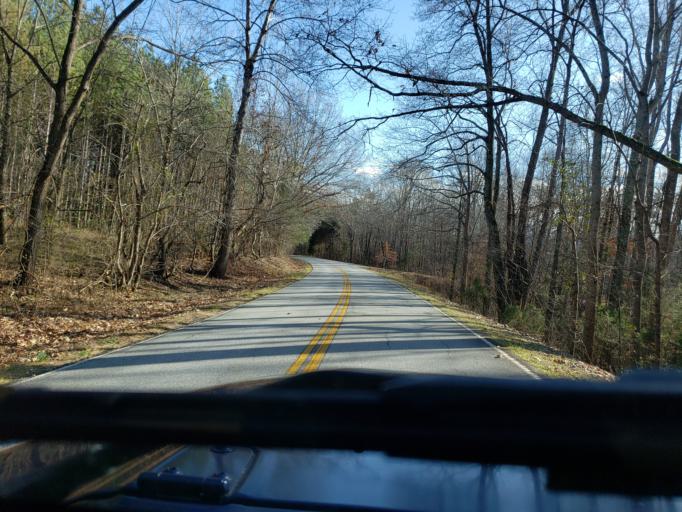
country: US
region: North Carolina
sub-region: Cleveland County
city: White Plains
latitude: 35.1597
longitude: -81.4049
